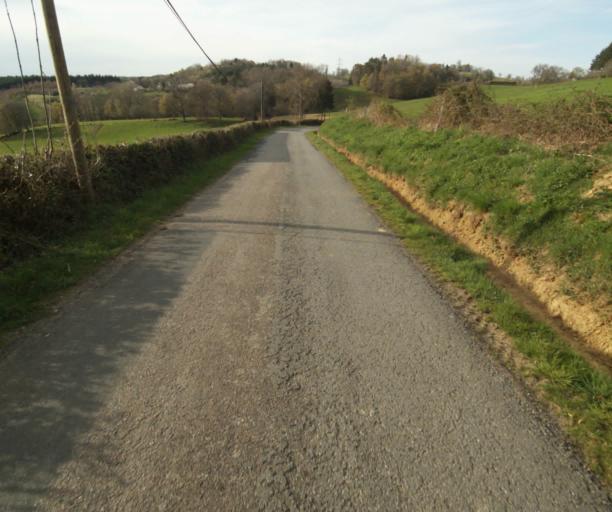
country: FR
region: Limousin
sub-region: Departement de la Correze
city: Naves
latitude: 45.3142
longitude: 1.7466
